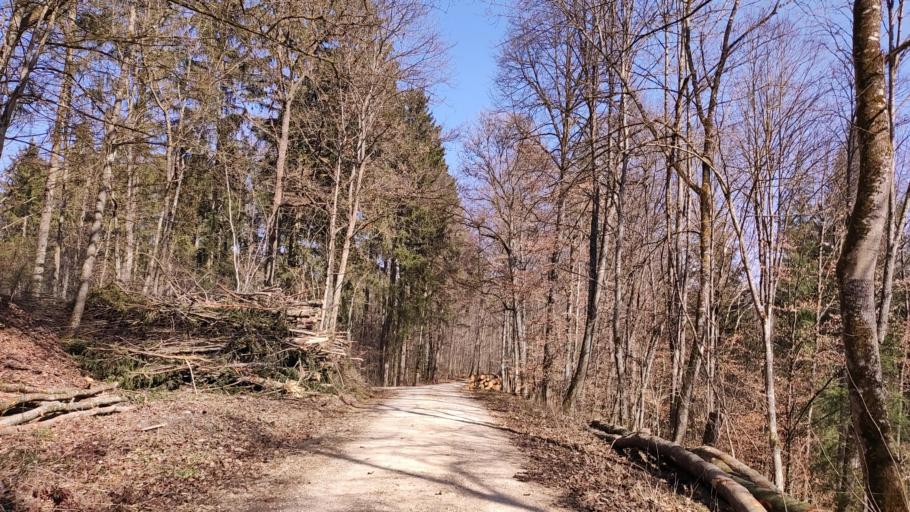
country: DE
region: Baden-Wuerttemberg
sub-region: Tuebingen Region
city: Borslingen
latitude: 48.5224
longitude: 10.0486
